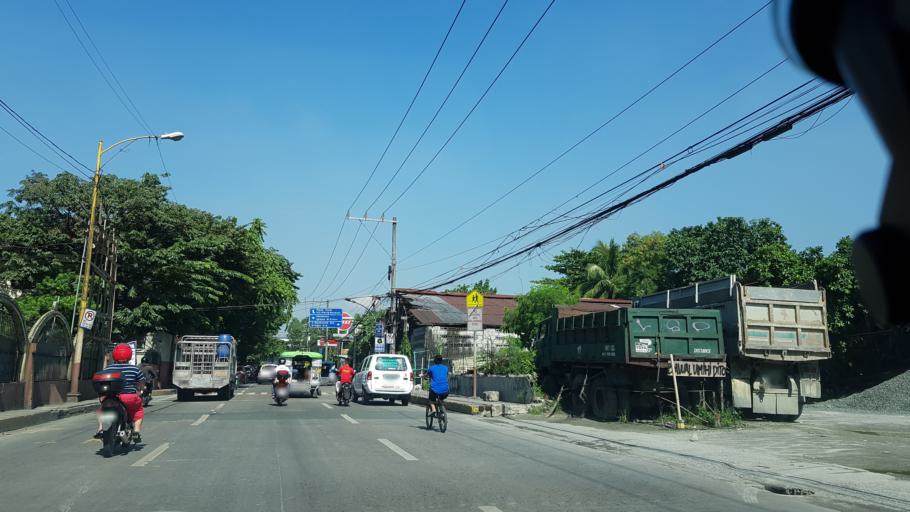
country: PH
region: Calabarzon
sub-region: Province of Rizal
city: Pateros
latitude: 14.5602
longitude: 121.0822
